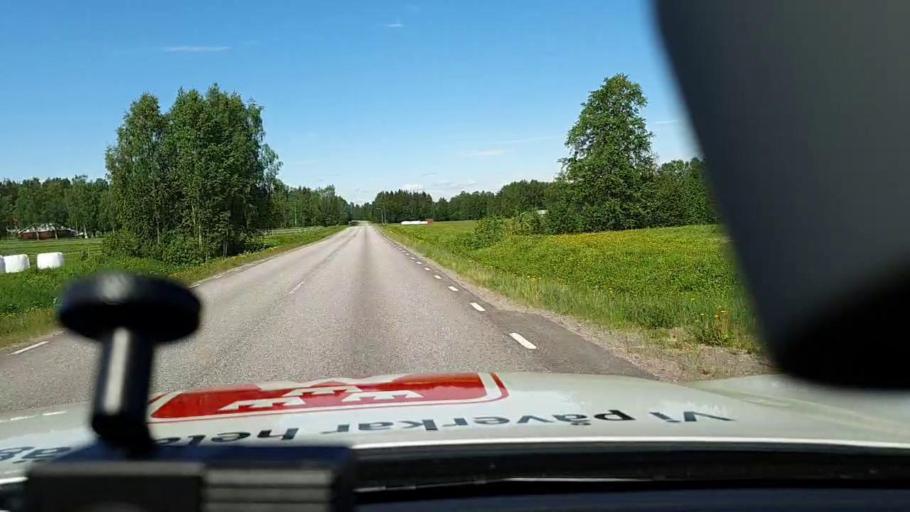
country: SE
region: Norrbotten
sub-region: Lulea Kommun
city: Sodra Sunderbyn
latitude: 65.6560
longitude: 21.8489
